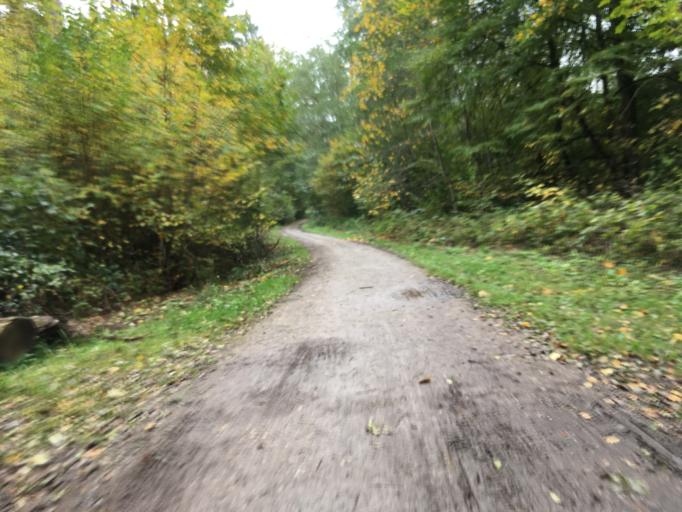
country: DE
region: Baden-Wuerttemberg
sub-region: Tuebingen Region
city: Gomaringen
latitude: 48.4823
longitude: 9.0767
